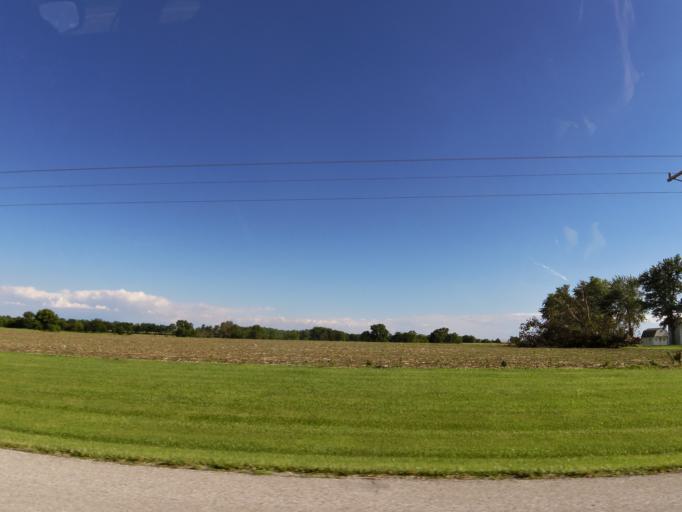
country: US
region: Missouri
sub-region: Marion County
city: Palmyra
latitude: 39.7437
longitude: -91.4689
